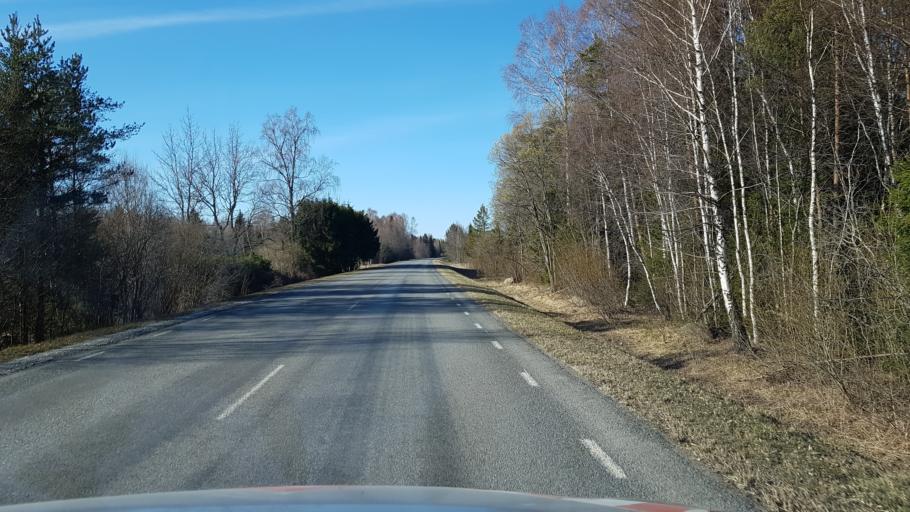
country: EE
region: Harju
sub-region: Keila linn
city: Keila
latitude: 59.2439
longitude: 24.4615
